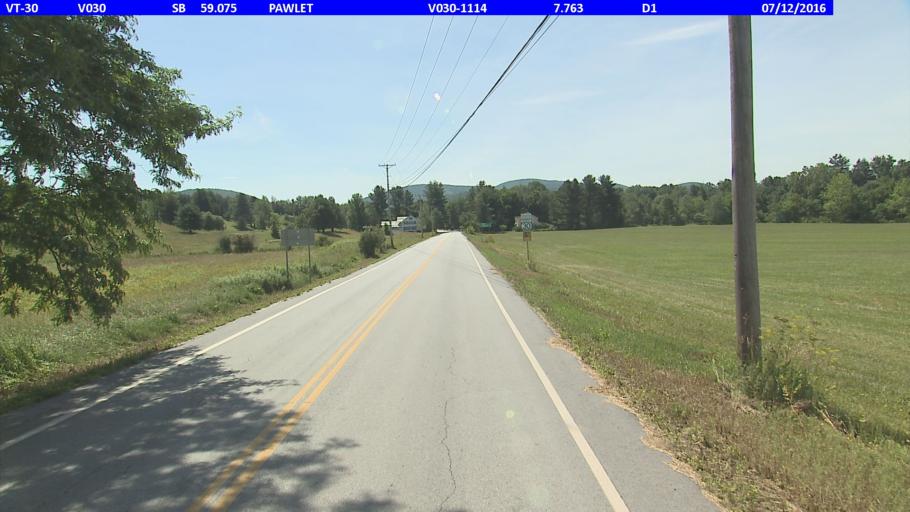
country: US
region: New York
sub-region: Washington County
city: Granville
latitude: 43.4008
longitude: -73.2257
